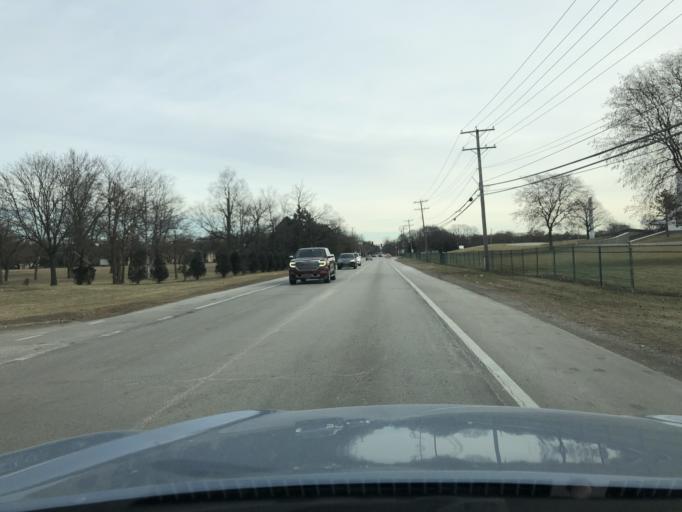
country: US
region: Illinois
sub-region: Cook County
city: Des Plaines
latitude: 42.0661
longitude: -87.8952
